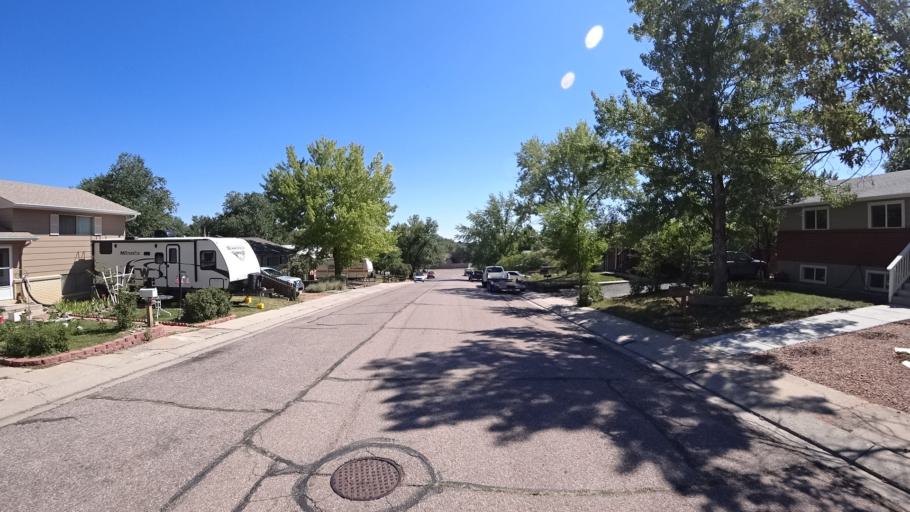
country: US
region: Colorado
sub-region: El Paso County
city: Colorado Springs
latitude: 38.8577
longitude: -104.8517
